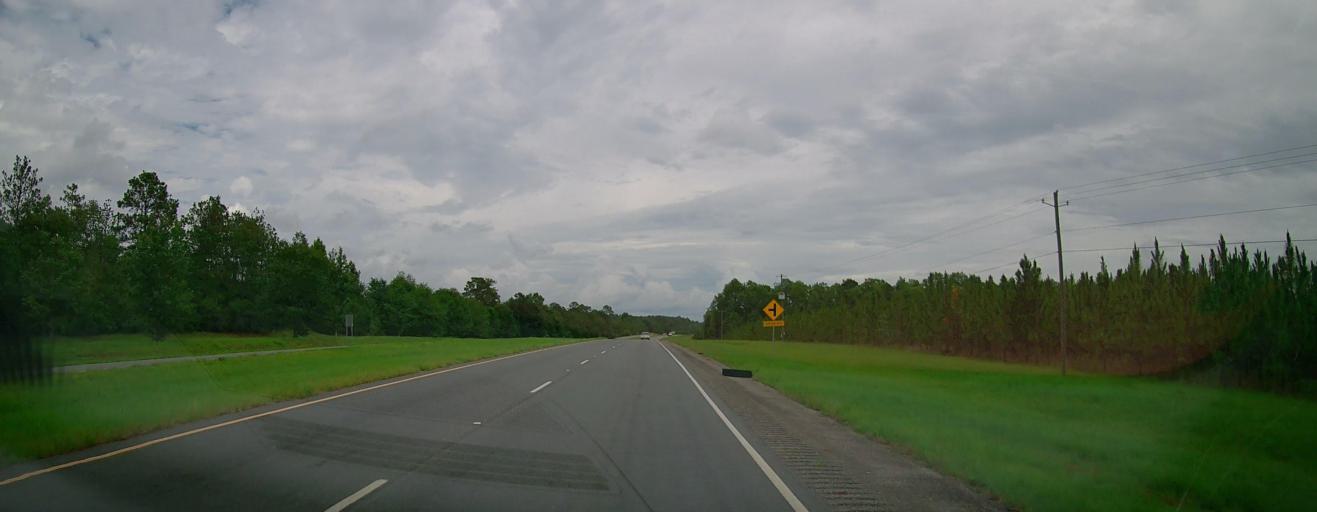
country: US
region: Georgia
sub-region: Telfair County
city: Helena
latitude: 32.1050
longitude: -82.9843
